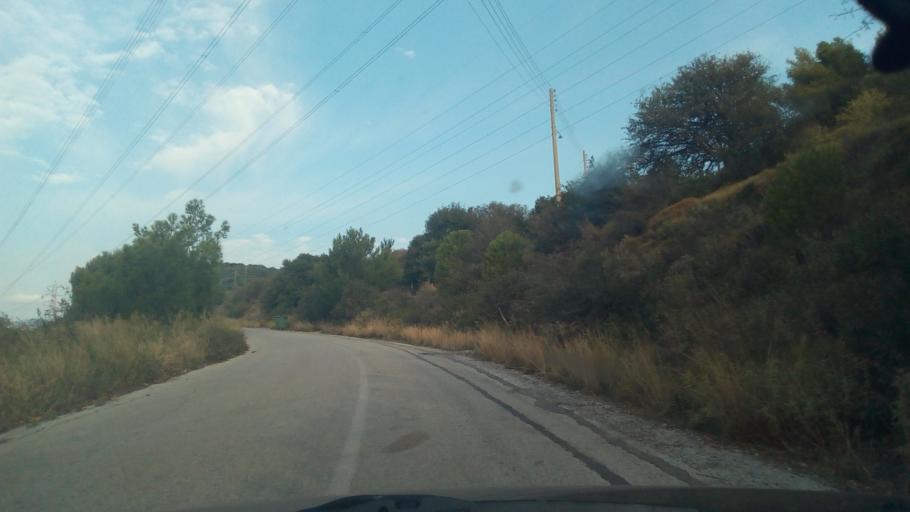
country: GR
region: West Greece
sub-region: Nomos Aitolias kai Akarnanias
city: Nafpaktos
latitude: 38.4130
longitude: 21.9272
